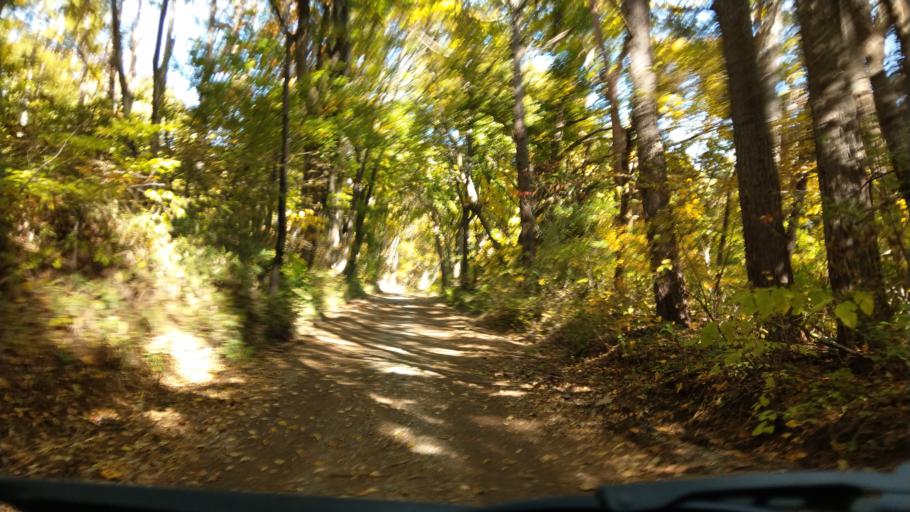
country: JP
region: Nagano
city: Komoro
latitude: 36.3638
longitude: 138.4519
